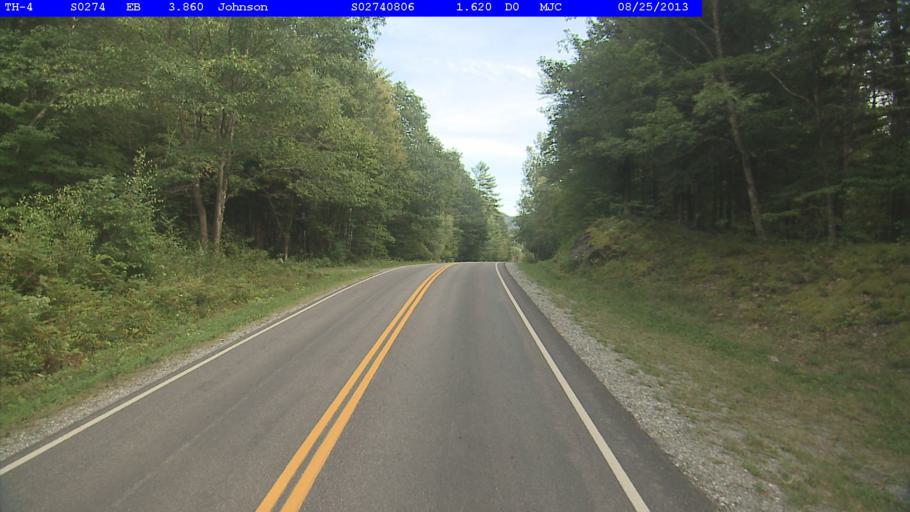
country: US
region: Vermont
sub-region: Lamoille County
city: Johnson
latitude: 44.6480
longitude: -72.7229
